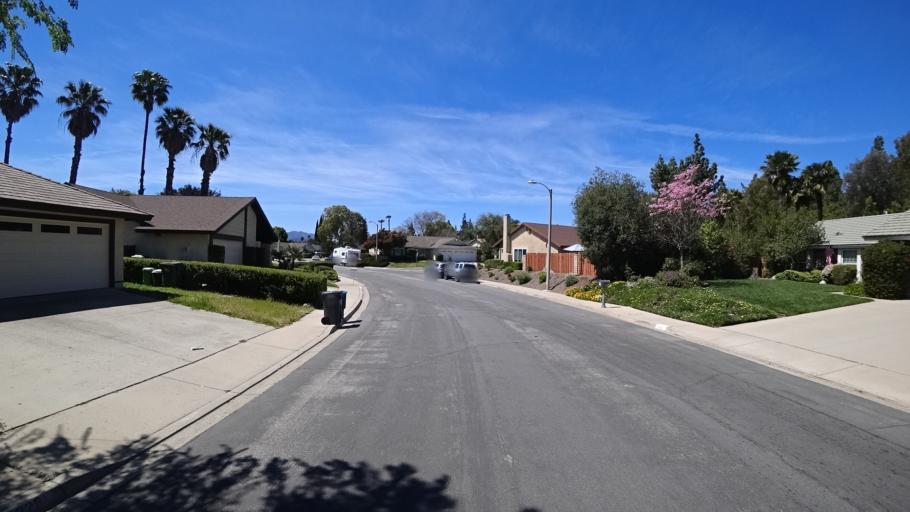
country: US
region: California
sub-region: Ventura County
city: Moorpark
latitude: 34.2265
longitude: -118.8705
